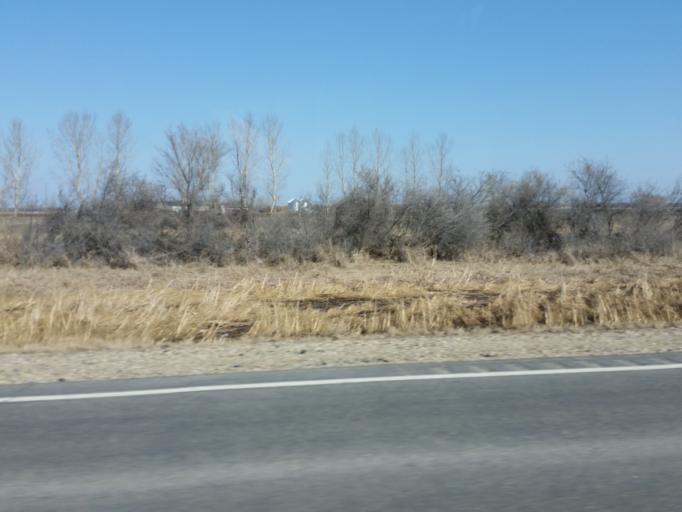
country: US
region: North Dakota
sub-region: Grand Forks County
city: Grand Forks Air Force Base
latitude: 48.1017
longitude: -97.2056
